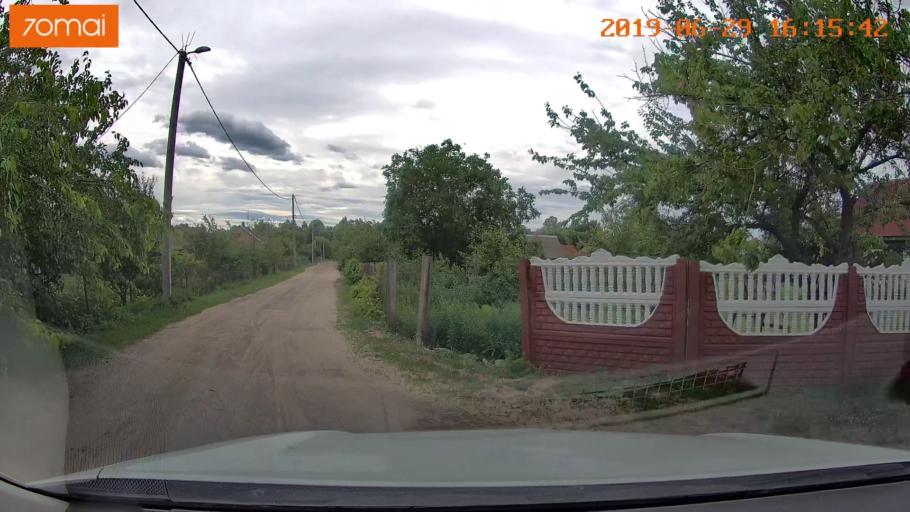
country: BY
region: Brest
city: Luninyets
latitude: 52.2018
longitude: 27.0128
